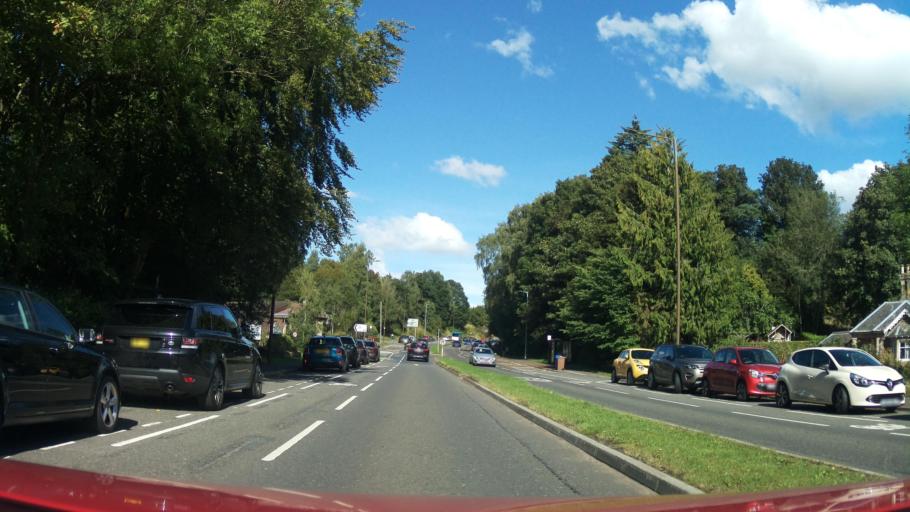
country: GB
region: Scotland
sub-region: Stirling
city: Dunblane
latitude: 56.1852
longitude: -3.9637
